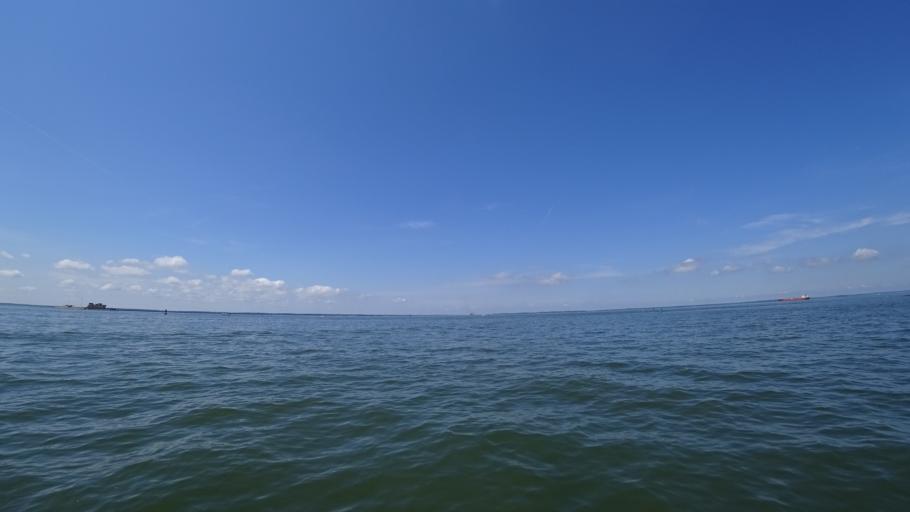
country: US
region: Virginia
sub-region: City of Newport News
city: Newport News
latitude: 36.9583
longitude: -76.4073
